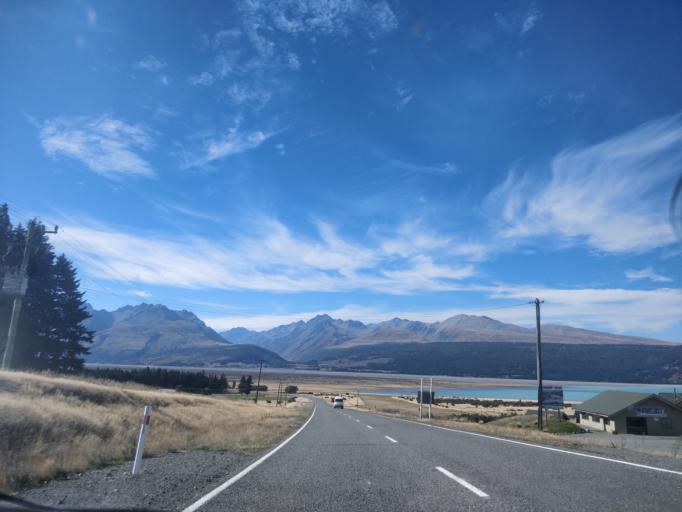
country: NZ
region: Canterbury
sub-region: Timaru District
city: Pleasant Point
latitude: -43.9121
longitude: 170.1200
